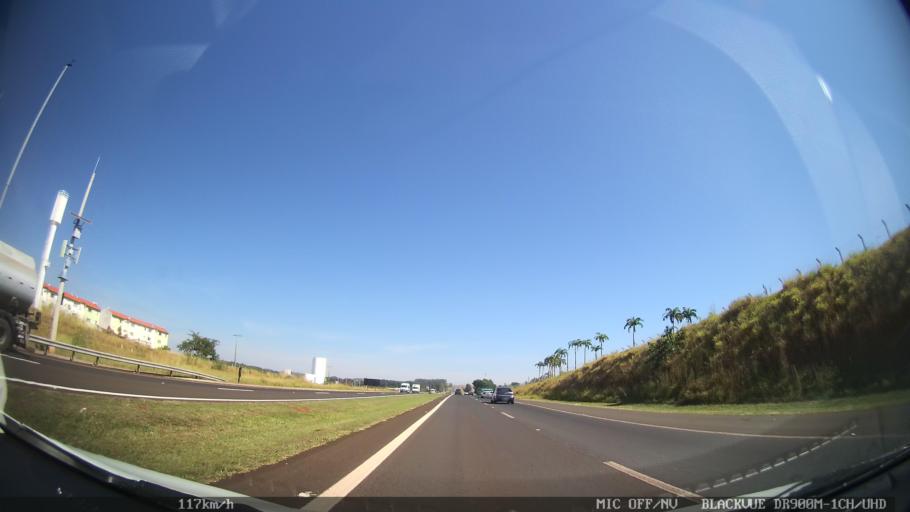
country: BR
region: Sao Paulo
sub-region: Ribeirao Preto
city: Ribeirao Preto
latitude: -21.1130
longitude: -47.8209
